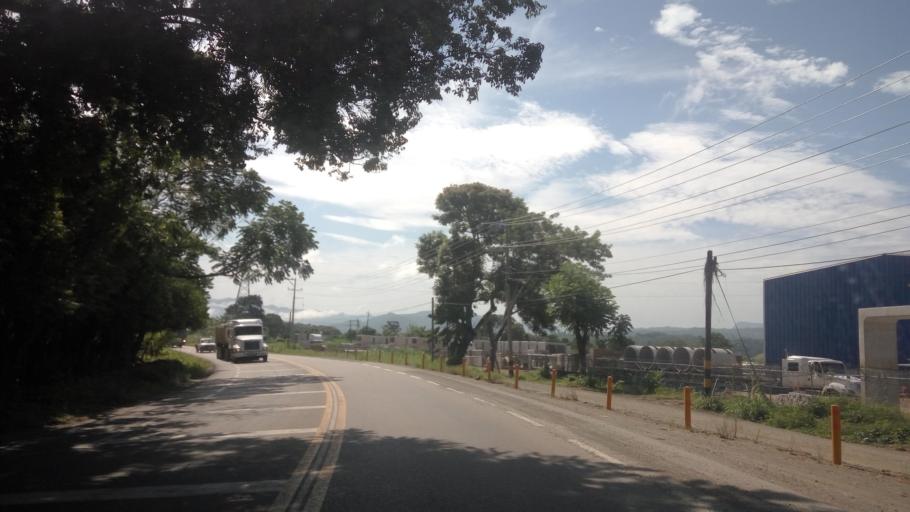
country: MX
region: Tabasco
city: Teapa
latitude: 17.5820
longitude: -92.9678
